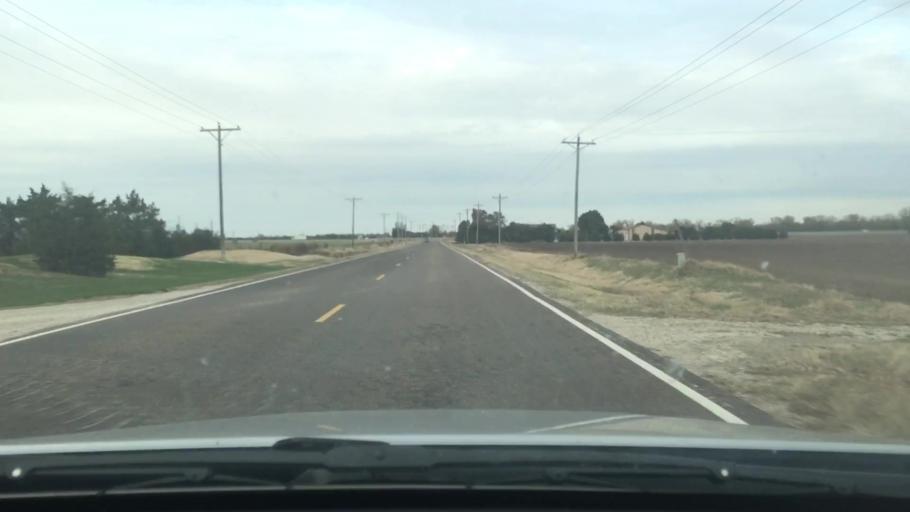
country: US
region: Kansas
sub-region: Sedgwick County
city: Colwich
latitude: 37.8178
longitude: -97.5184
